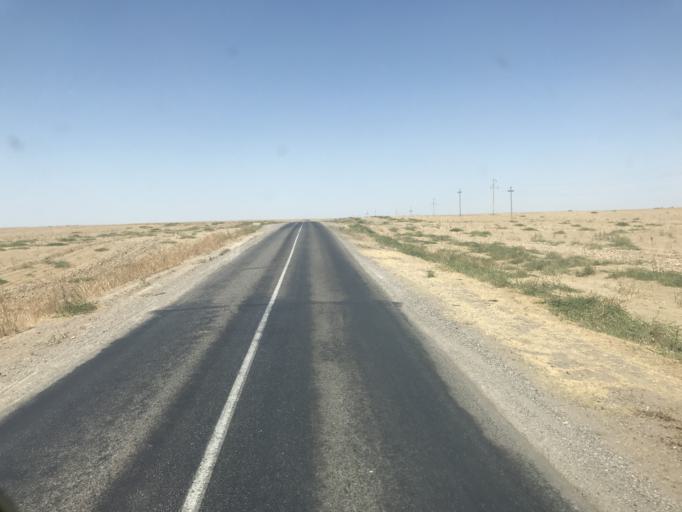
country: UZ
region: Toshkent
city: Chinoz
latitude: 41.1423
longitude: 68.6995
